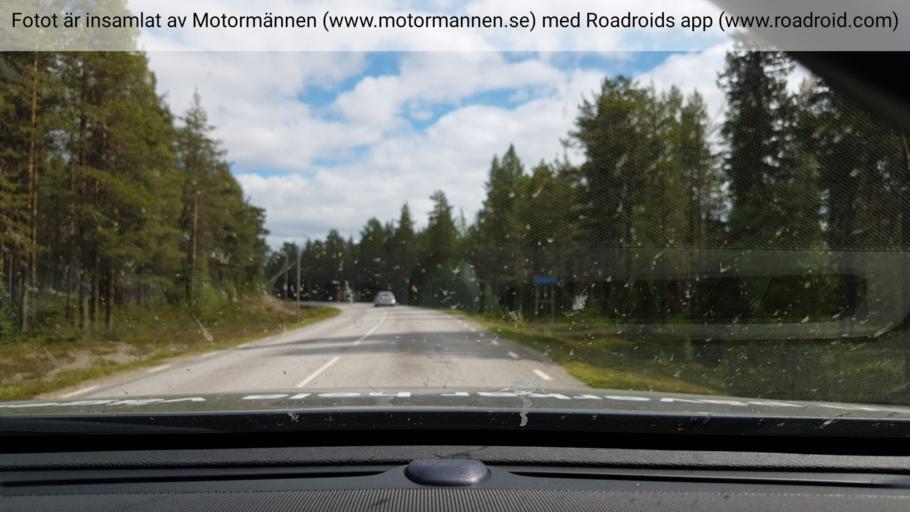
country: SE
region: Vaesterbotten
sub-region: Sorsele Kommun
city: Sorsele
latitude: 65.6885
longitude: 17.3161
